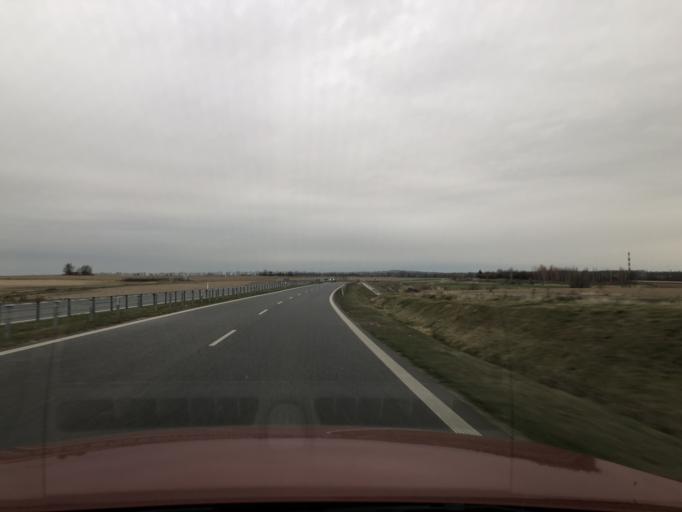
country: PL
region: Lower Silesian Voivodeship
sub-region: Powiat swidnicki
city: Swidnica
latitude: 50.8512
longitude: 16.4378
